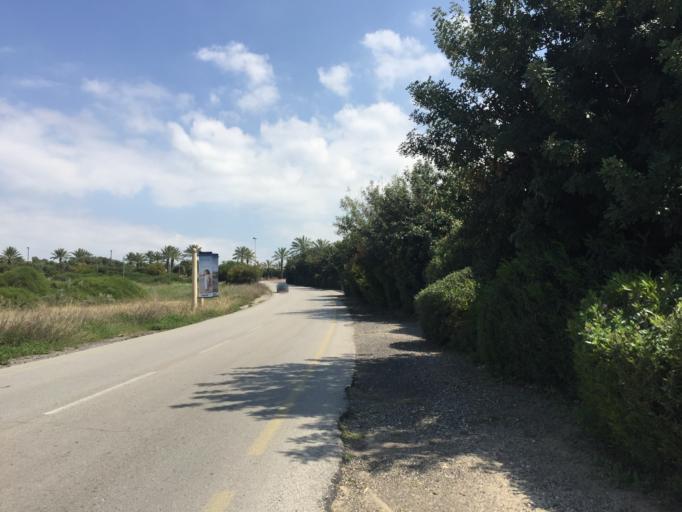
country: IL
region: Haifa
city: Qesarya
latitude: 32.4905
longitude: 34.9013
